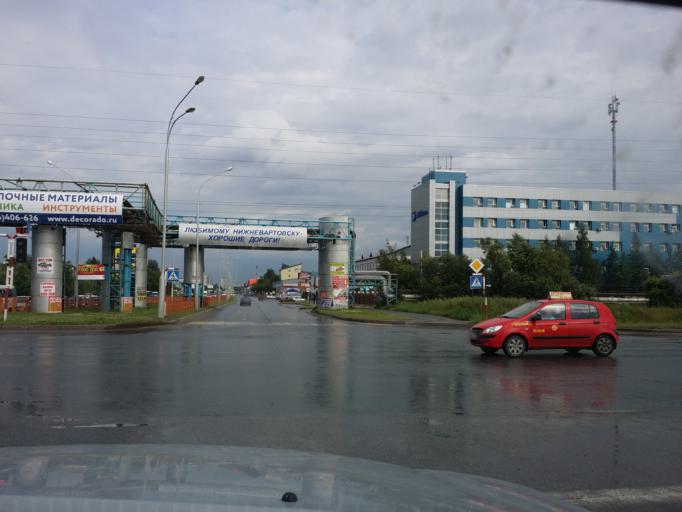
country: RU
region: Khanty-Mansiyskiy Avtonomnyy Okrug
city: Nizhnevartovsk
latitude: 60.9389
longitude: 76.5302
